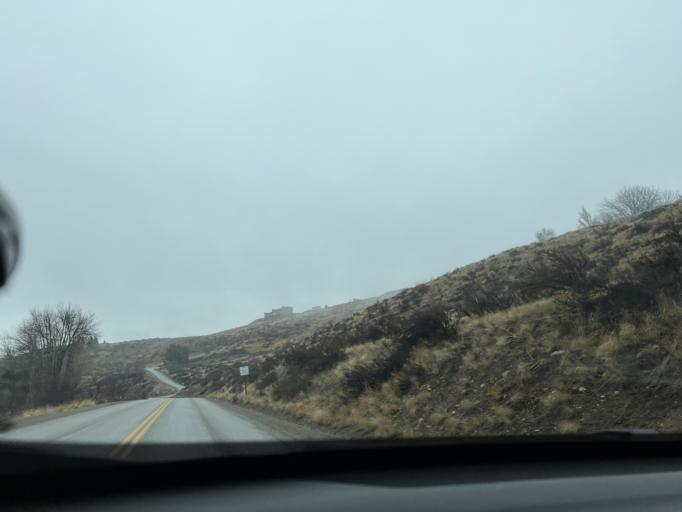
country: US
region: Washington
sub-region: Okanogan County
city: Brewster
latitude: 48.4847
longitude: -120.1779
